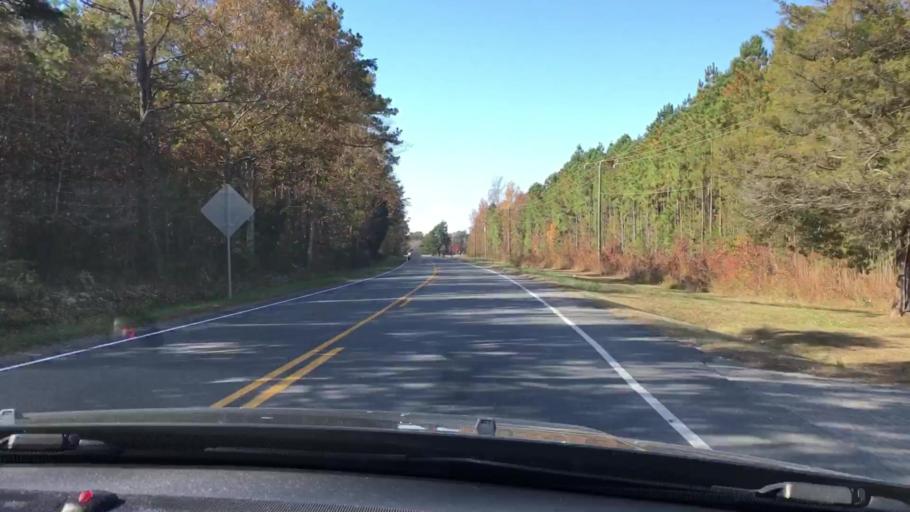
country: US
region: Virginia
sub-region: King William County
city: King William
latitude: 37.6579
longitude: -76.9523
